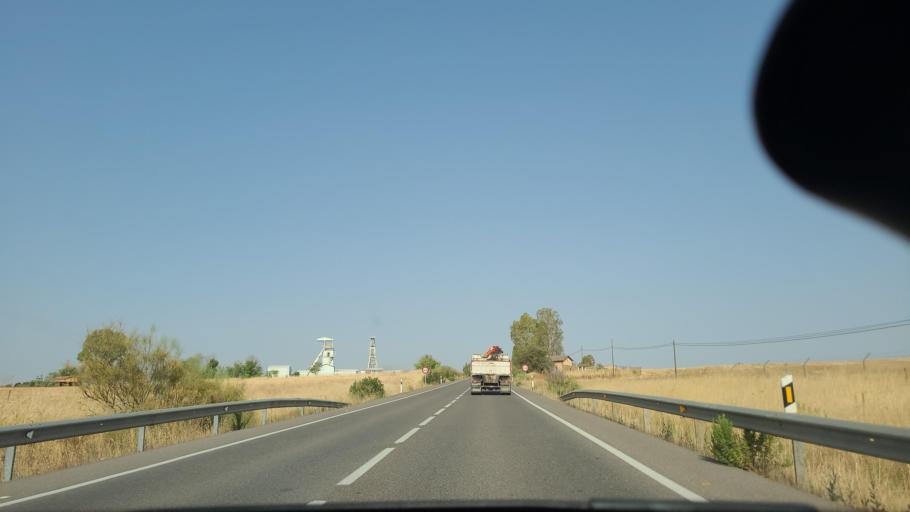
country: ES
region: Andalusia
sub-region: Province of Cordoba
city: Penarroya-Pueblonuevo
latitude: 38.2995
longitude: -5.3098
